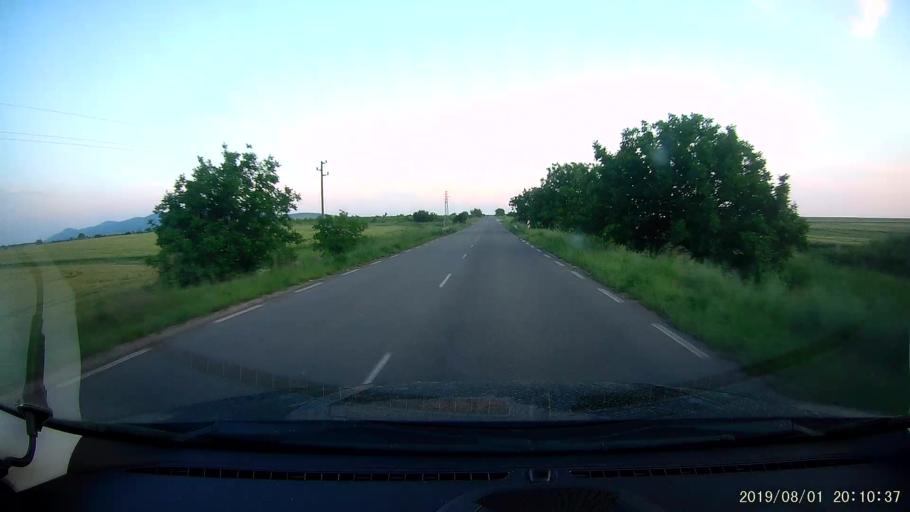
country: BG
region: Yambol
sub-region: Obshtina Yambol
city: Yambol
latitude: 42.4780
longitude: 26.6009
